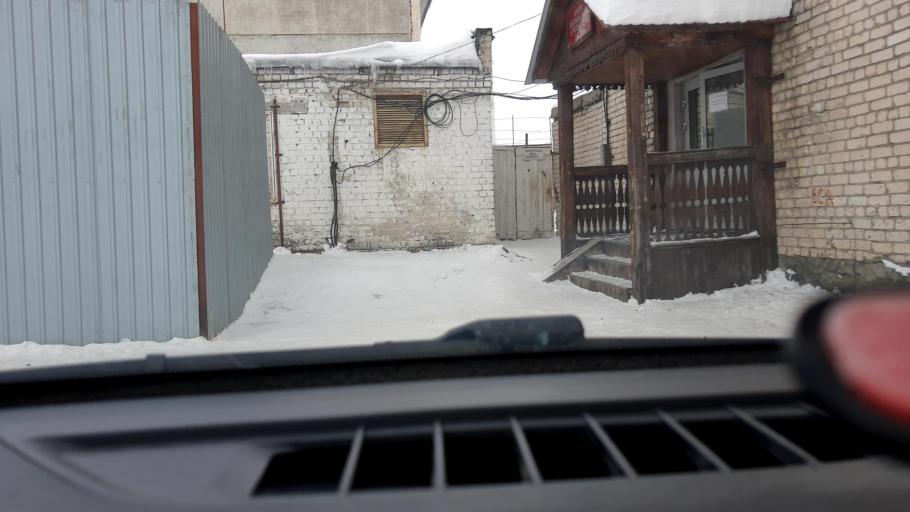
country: RU
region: Nizjnij Novgorod
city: Babino
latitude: 56.2655
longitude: 43.6058
